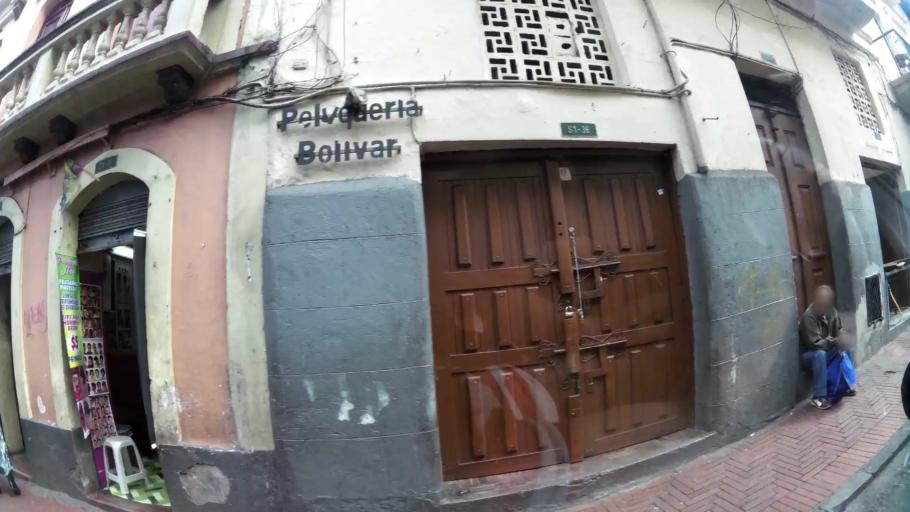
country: EC
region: Pichincha
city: Quito
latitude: -0.2210
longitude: -78.5175
